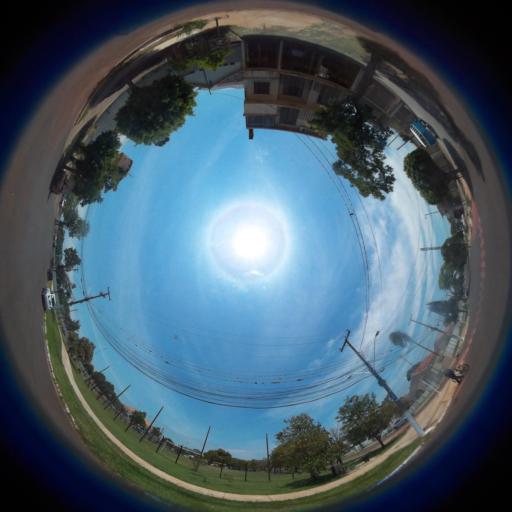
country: BR
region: Mato Grosso do Sul
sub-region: Ponta Pora
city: Ponta Pora
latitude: -22.5393
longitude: -55.7221
